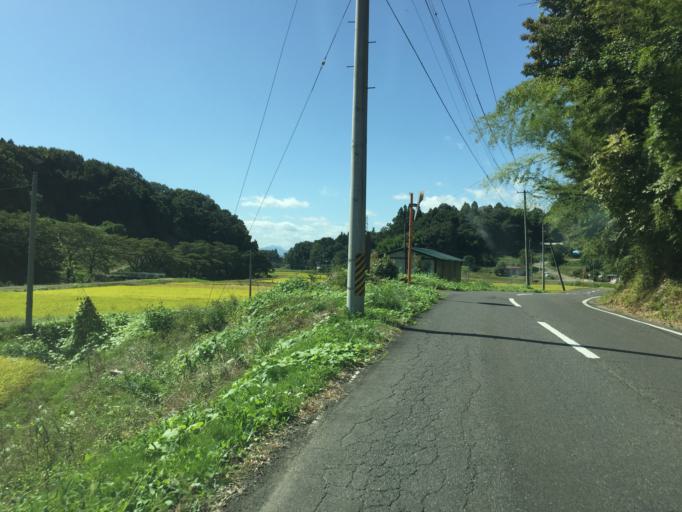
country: JP
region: Fukushima
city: Sukagawa
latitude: 37.2832
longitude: 140.4376
